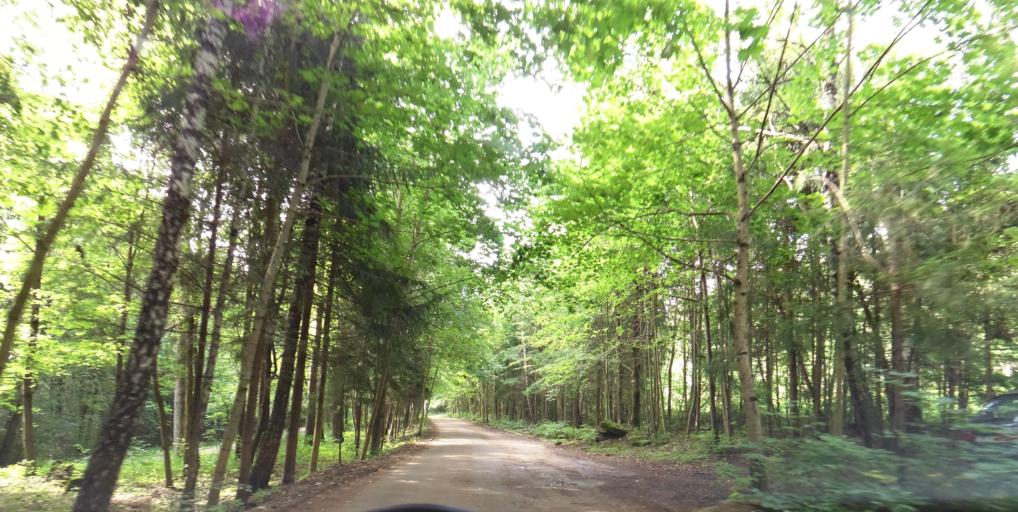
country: LT
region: Vilnius County
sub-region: Vilnius
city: Fabijoniskes
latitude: 54.7380
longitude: 25.2833
